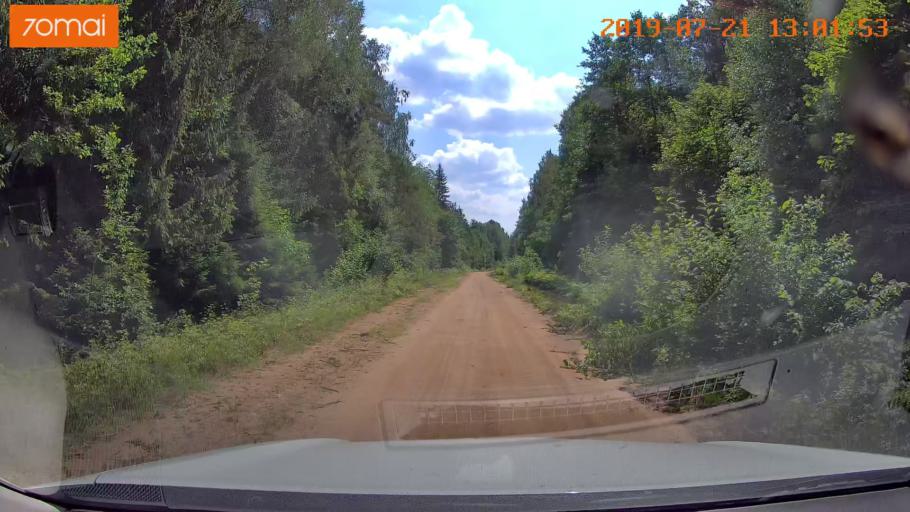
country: BY
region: Grodnenskaya
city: Lyubcha
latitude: 53.8504
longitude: 26.0226
